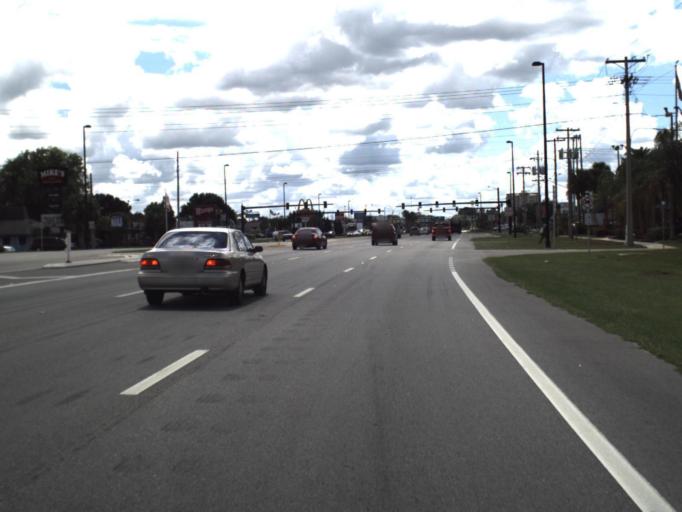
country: US
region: Florida
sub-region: Polk County
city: Bartow
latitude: 27.9109
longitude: -81.8437
